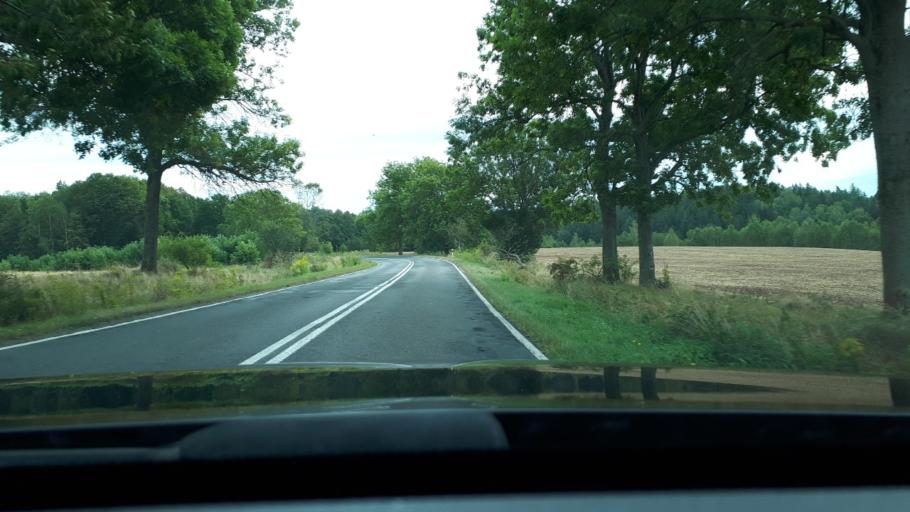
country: PL
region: Lower Silesian Voivodeship
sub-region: Powiat lwowecki
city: Lwowek Slaski
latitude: 51.0984
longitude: 15.5092
